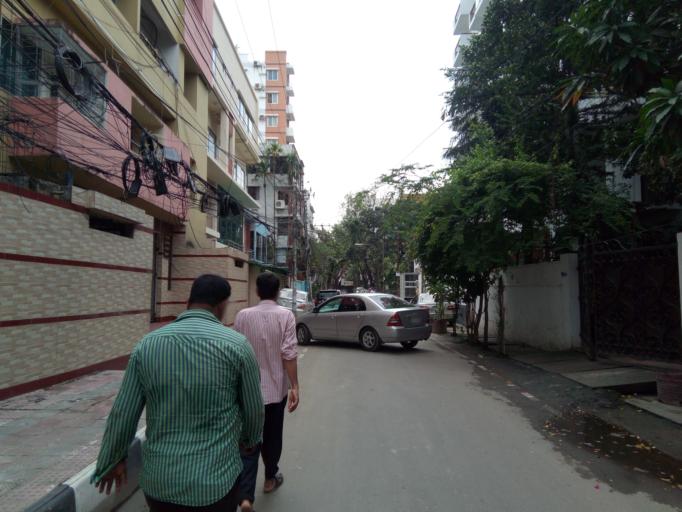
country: BD
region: Dhaka
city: Paltan
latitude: 23.7921
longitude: 90.4093
